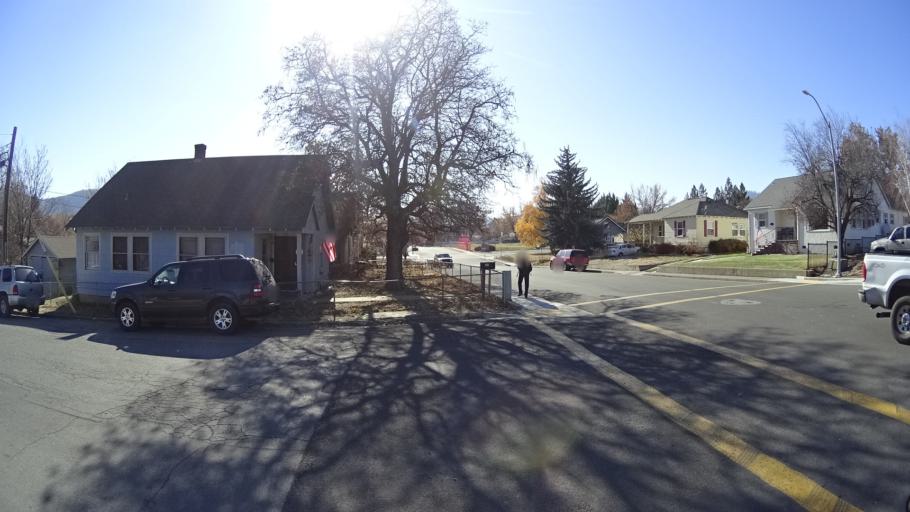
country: US
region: California
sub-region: Siskiyou County
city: Yreka
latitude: 41.7393
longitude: -122.6357
